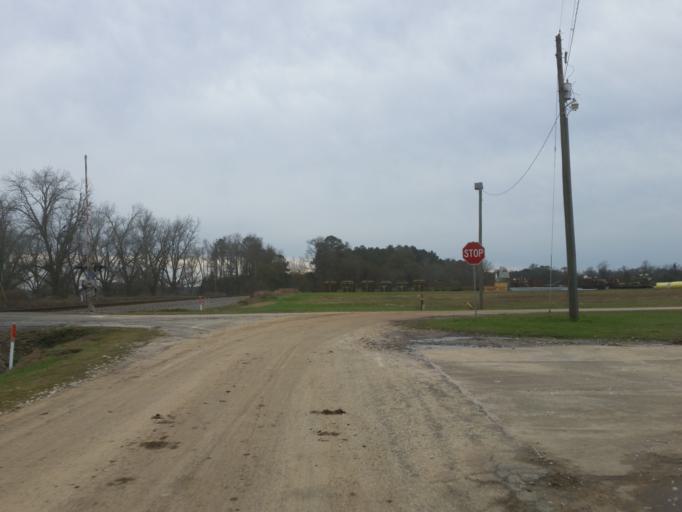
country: US
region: Georgia
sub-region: Dooly County
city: Vienna
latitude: 32.1539
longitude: -83.7720
